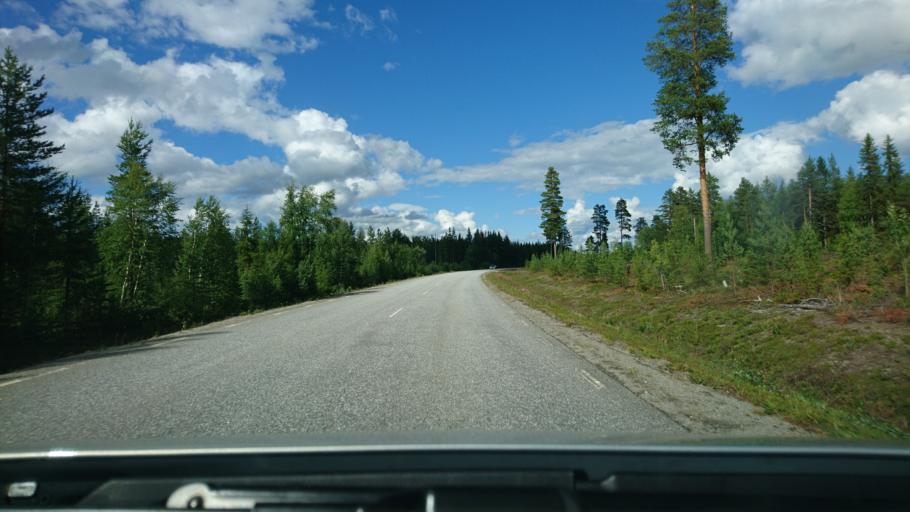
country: SE
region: Vaesterbotten
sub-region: Asele Kommun
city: Asele
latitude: 63.9985
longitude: 17.2660
